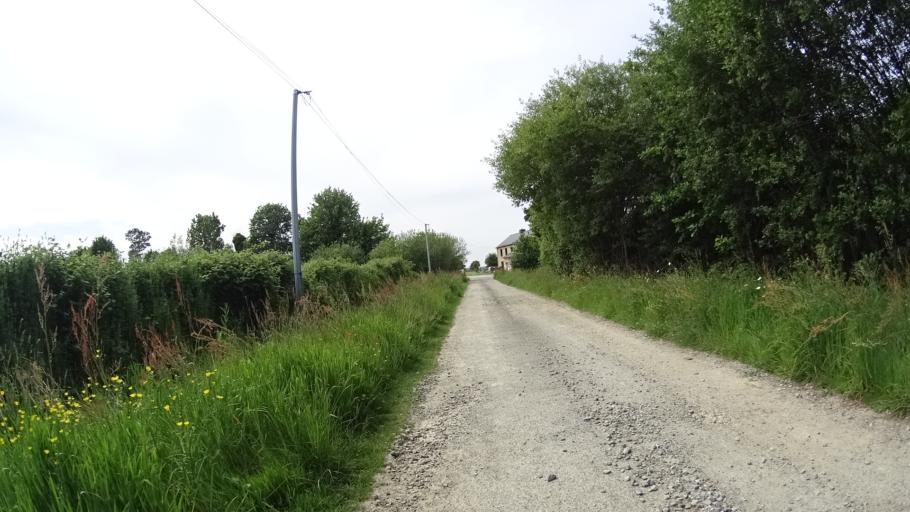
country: FR
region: Brittany
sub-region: Departement d'Ille-et-Vilaine
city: La Meziere
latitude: 48.2201
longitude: -1.7643
